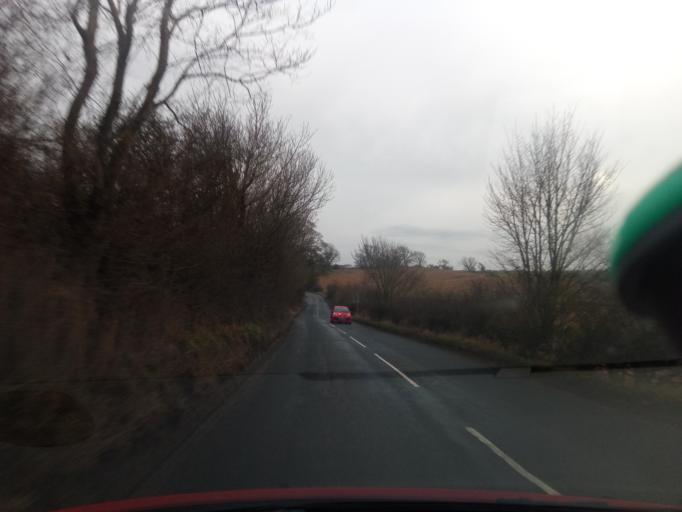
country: GB
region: England
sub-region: Northumberland
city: Birtley
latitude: 55.0504
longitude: -2.1585
